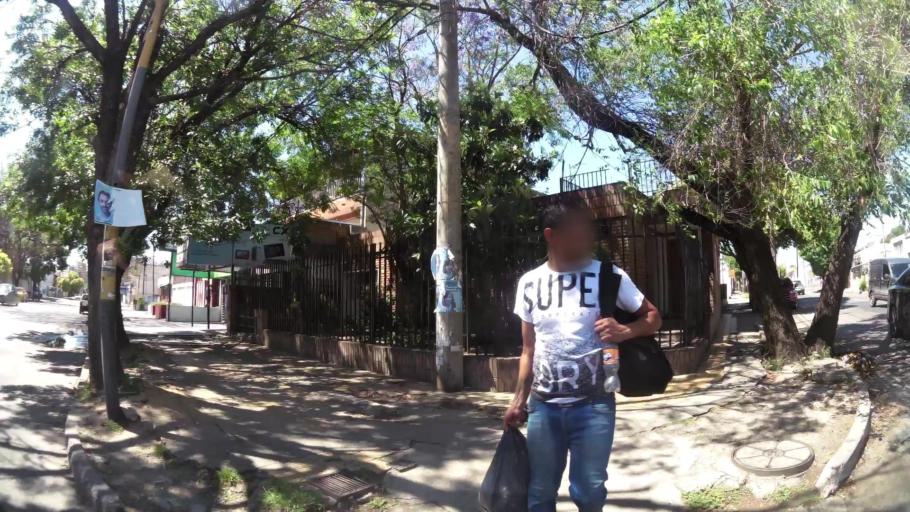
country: AR
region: Cordoba
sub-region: Departamento de Capital
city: Cordoba
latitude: -31.4212
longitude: -64.2087
